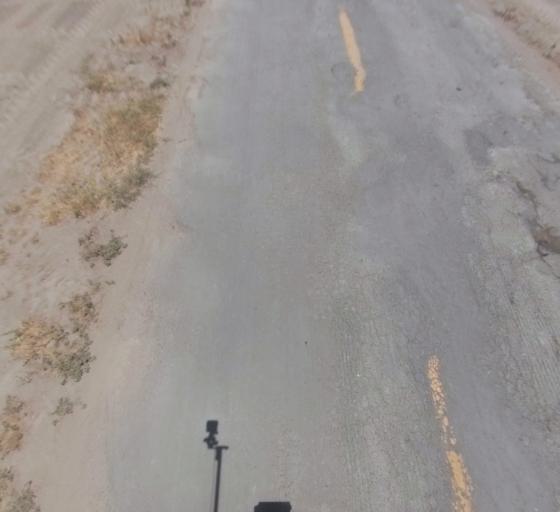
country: US
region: California
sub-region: Madera County
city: Parkwood
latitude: 36.8658
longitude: -120.1666
